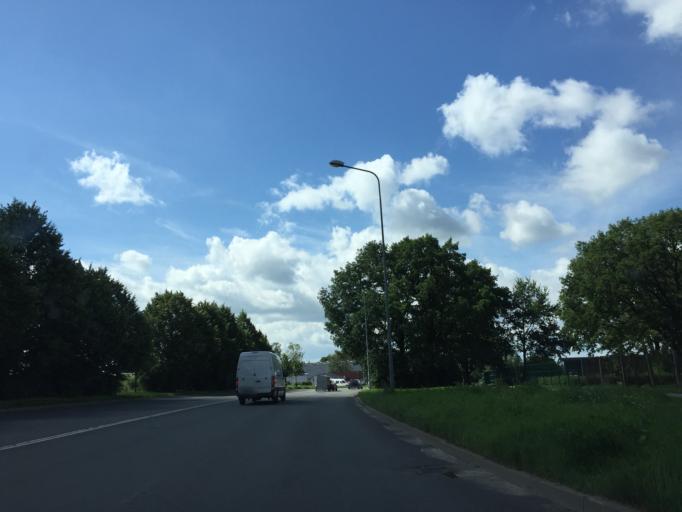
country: LV
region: Stopini
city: Ulbroka
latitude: 56.9574
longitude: 24.2277
